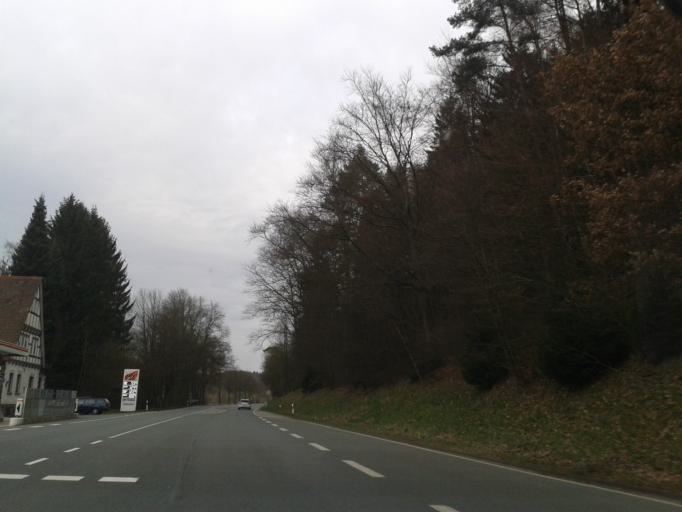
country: DE
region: Hesse
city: Frankenberg
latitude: 51.0733
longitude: 8.8143
